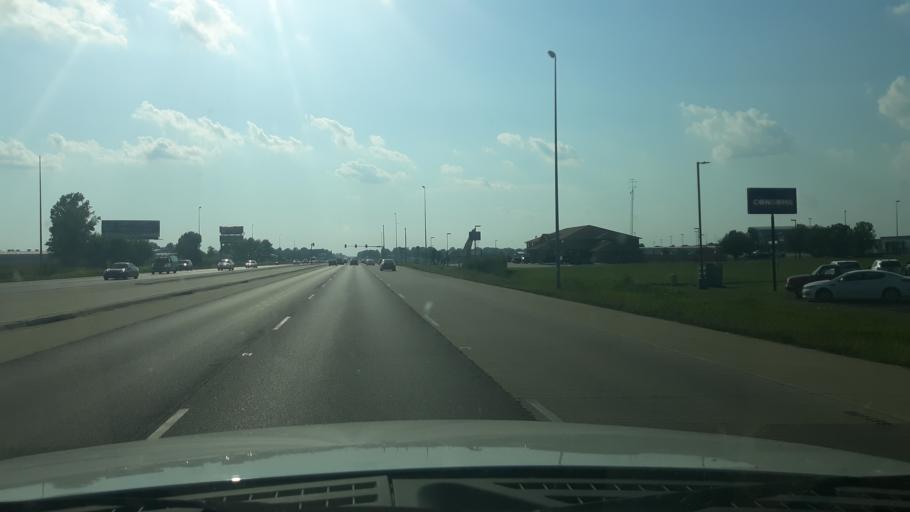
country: US
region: Illinois
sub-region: Williamson County
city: Energy
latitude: 37.7451
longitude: -89.0070
